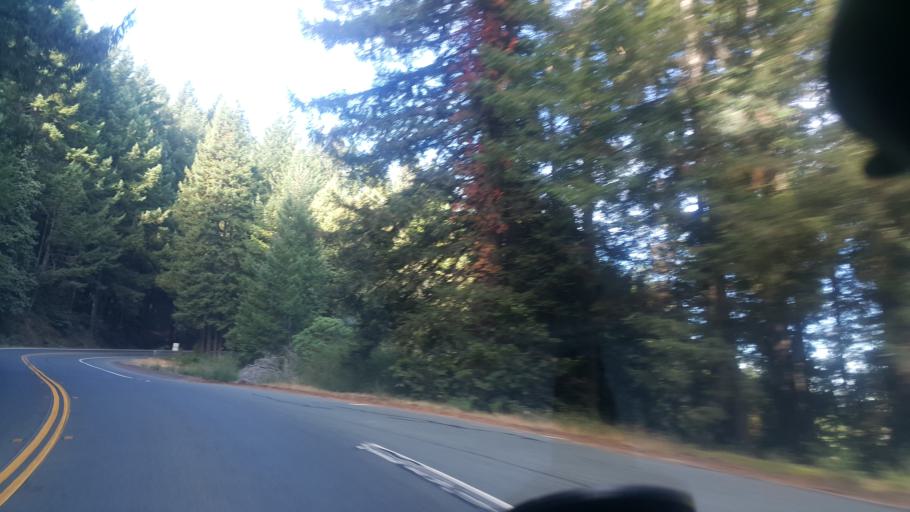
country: US
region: California
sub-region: Mendocino County
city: Brooktrails
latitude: 39.3931
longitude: -123.4605
